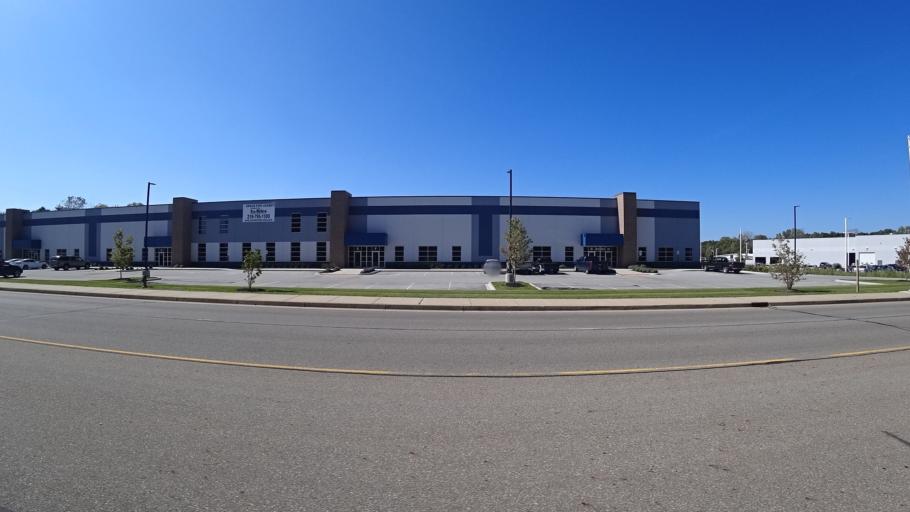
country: US
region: Indiana
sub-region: LaPorte County
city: Michigan City
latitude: 41.6784
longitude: -86.8845
